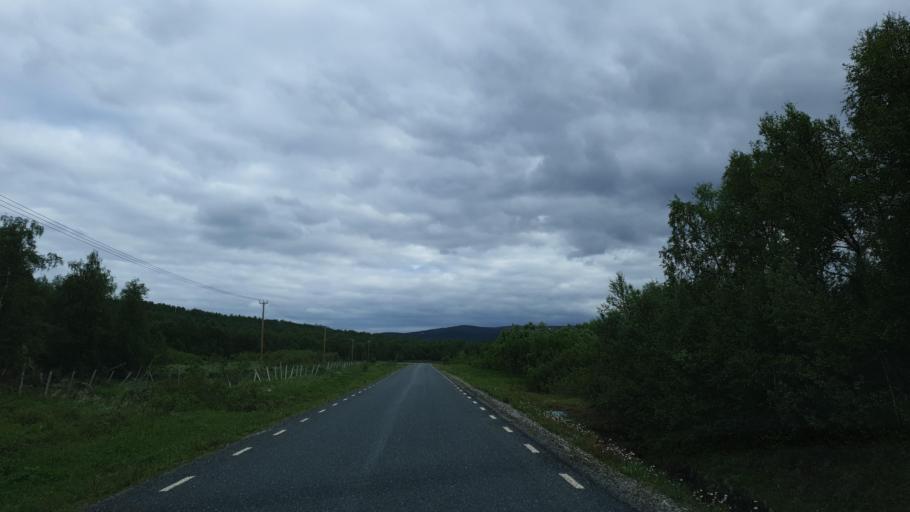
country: NO
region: Nordland
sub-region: Hattfjelldal
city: Hattfjelldal
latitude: 65.4244
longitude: 14.6575
